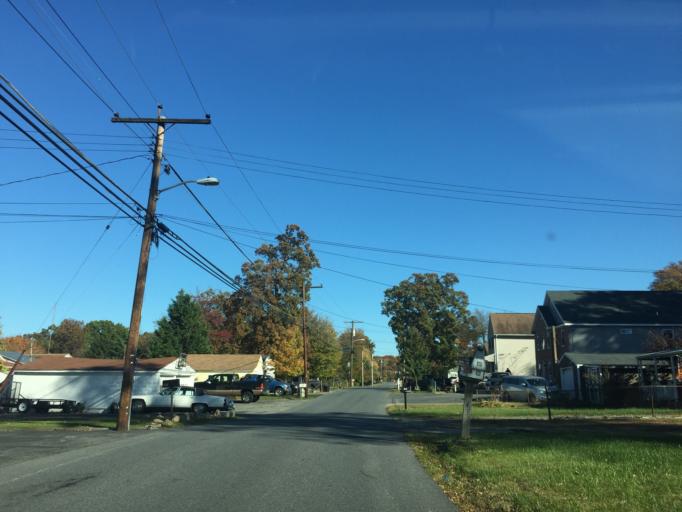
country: US
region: Maryland
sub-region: Baltimore County
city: Essex
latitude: 39.2719
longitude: -76.4761
